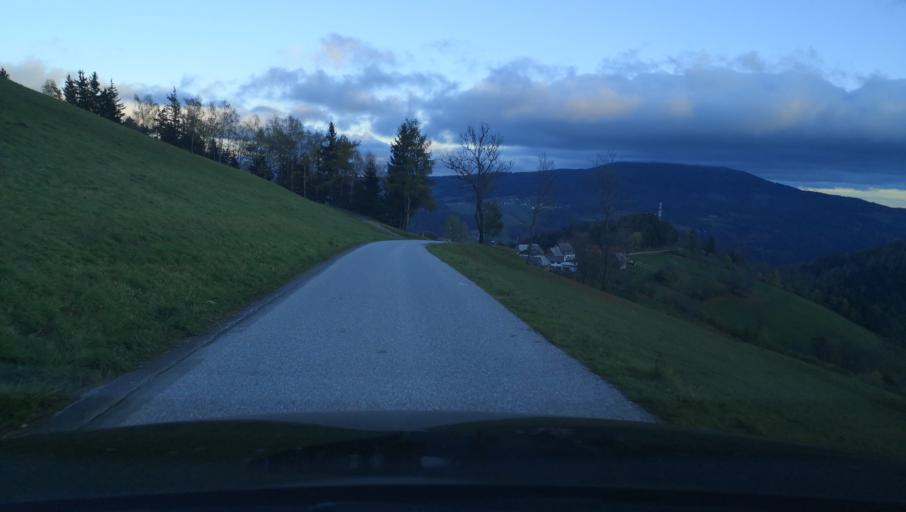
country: AT
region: Styria
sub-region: Politischer Bezirk Weiz
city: Birkfeld
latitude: 47.3395
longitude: 15.6561
